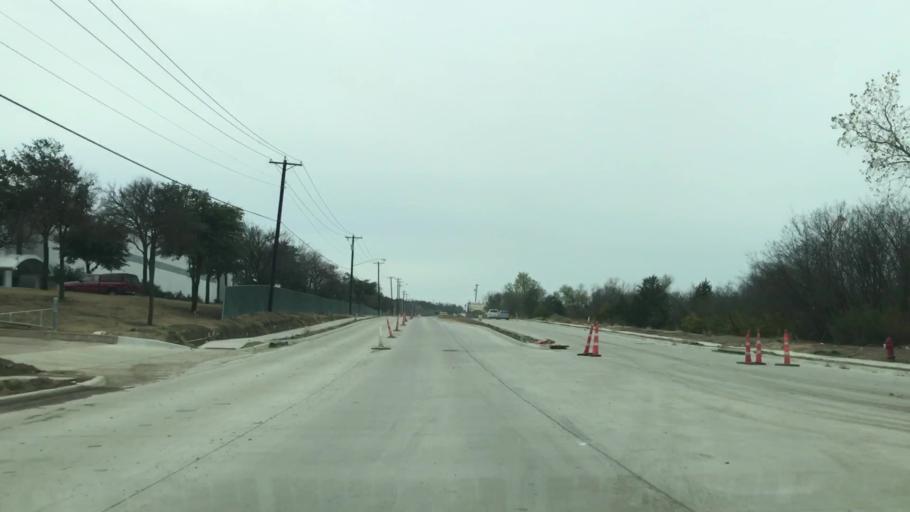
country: US
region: Texas
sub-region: Dallas County
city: Cockrell Hill
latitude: 32.7615
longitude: -96.9022
